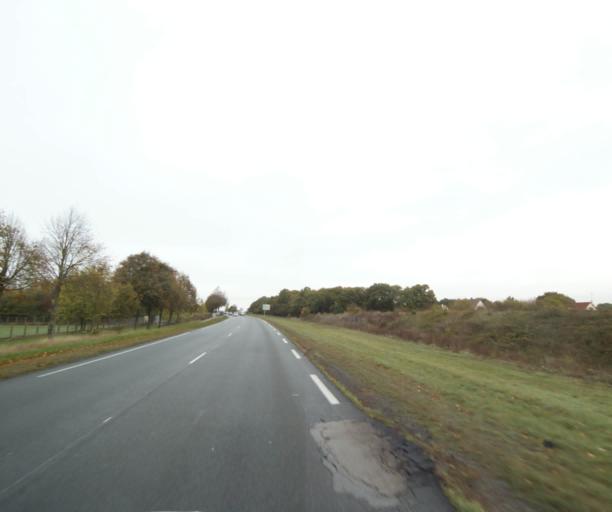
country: FR
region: Centre
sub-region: Departement d'Eure-et-Loir
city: Luray
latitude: 48.7231
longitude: 1.3859
